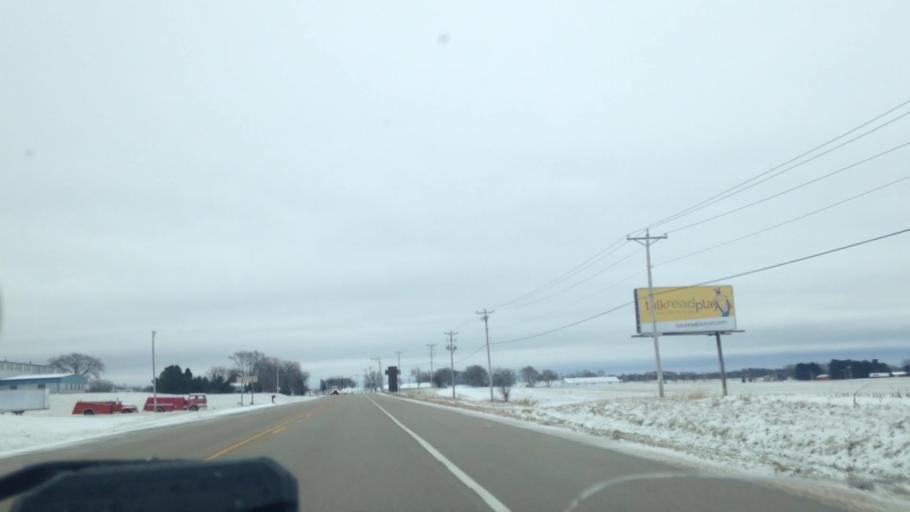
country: US
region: Wisconsin
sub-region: Dodge County
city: Beaver Dam
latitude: 43.4442
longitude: -88.7686
